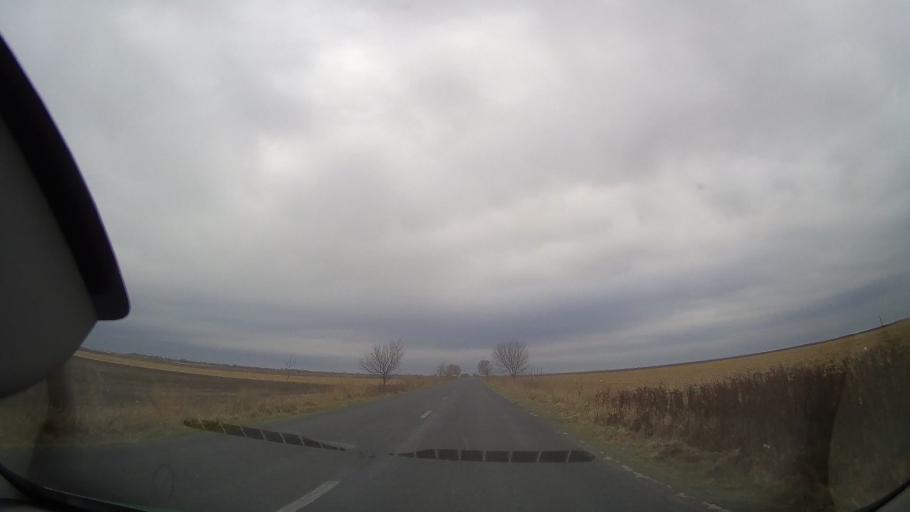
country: RO
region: Buzau
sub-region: Comuna Padina
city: Padina
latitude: 44.7914
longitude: 27.1432
